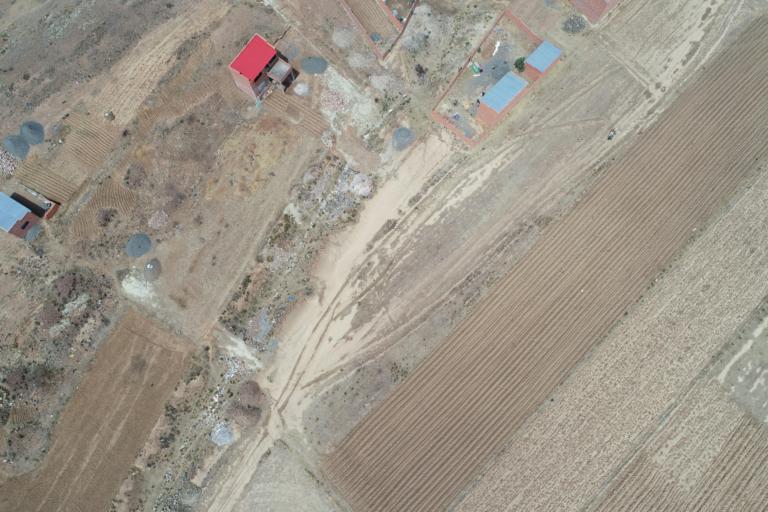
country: BO
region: La Paz
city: Achacachi
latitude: -16.0545
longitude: -68.6762
